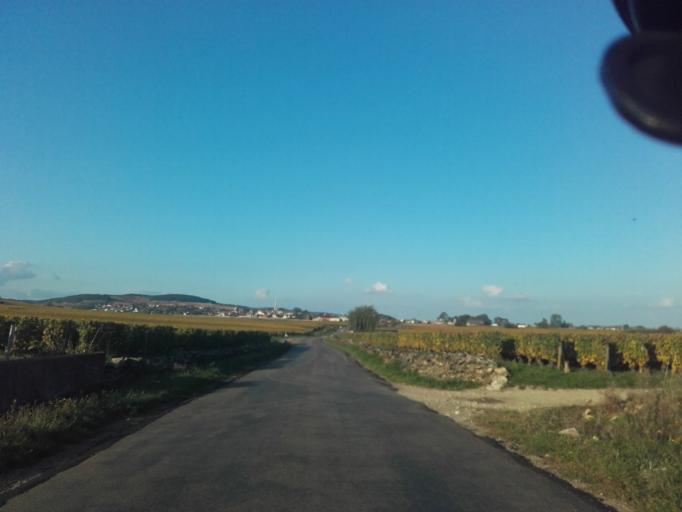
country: FR
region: Bourgogne
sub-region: Departement de la Cote-d'Or
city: Meursault
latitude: 46.9623
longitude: 4.7609
